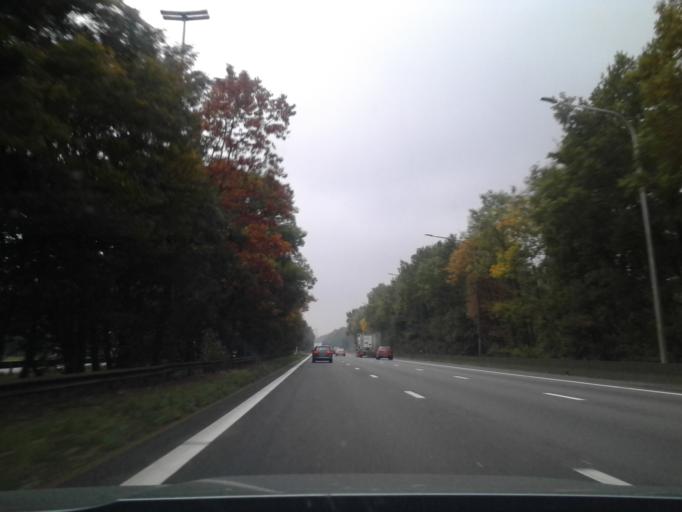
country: BE
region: Wallonia
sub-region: Province du Hainaut
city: Roeulx
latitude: 50.4986
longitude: 4.1402
